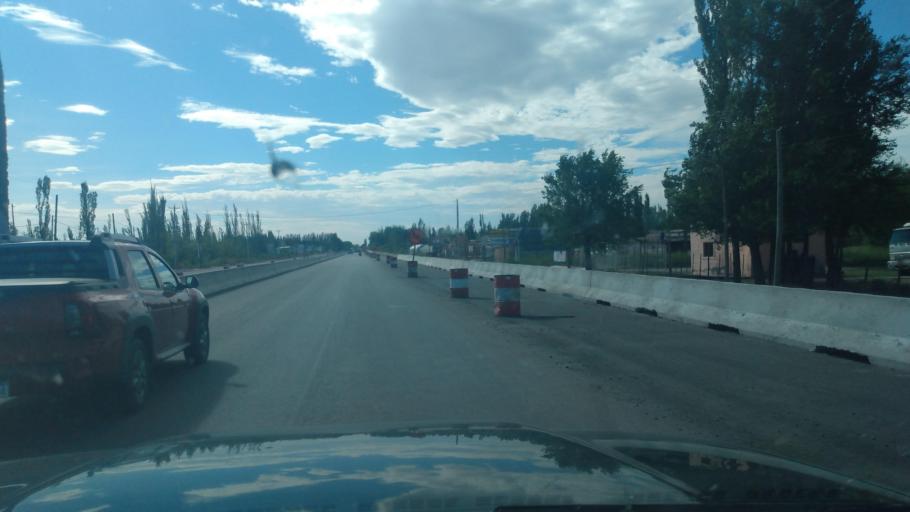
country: AR
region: Rio Negro
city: Cipolletti
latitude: -38.9634
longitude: -67.9698
